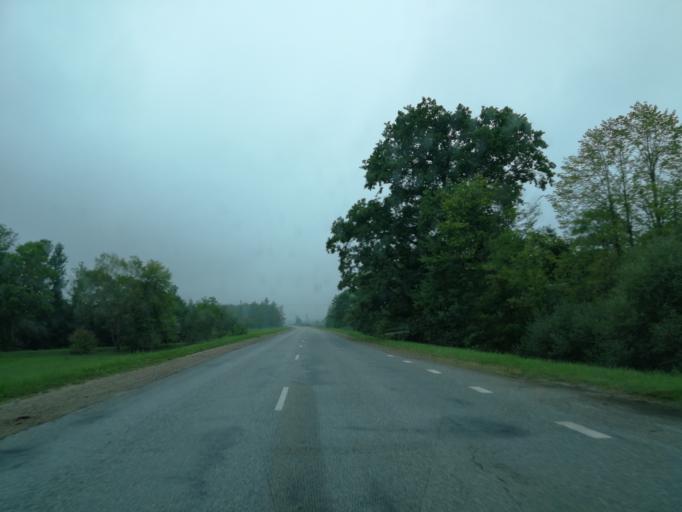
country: LV
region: Varkava
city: Vecvarkava
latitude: 56.3127
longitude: 26.5361
